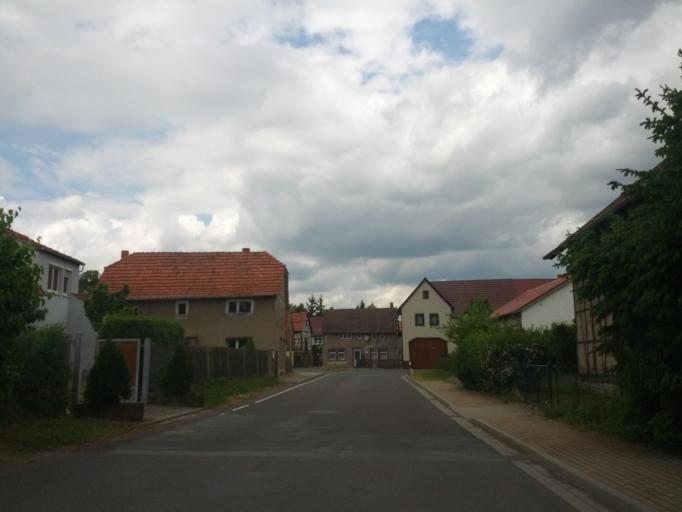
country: DE
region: Thuringia
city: Friedrichswerth
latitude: 50.9914
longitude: 10.5419
